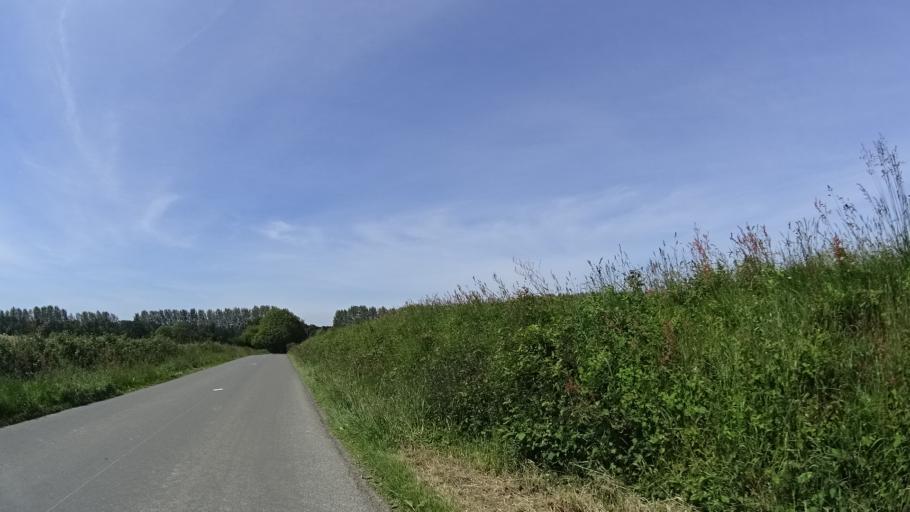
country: FR
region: Brittany
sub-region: Departement d'Ille-et-Vilaine
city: Saint-Gilles
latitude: 48.1948
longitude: -1.8402
